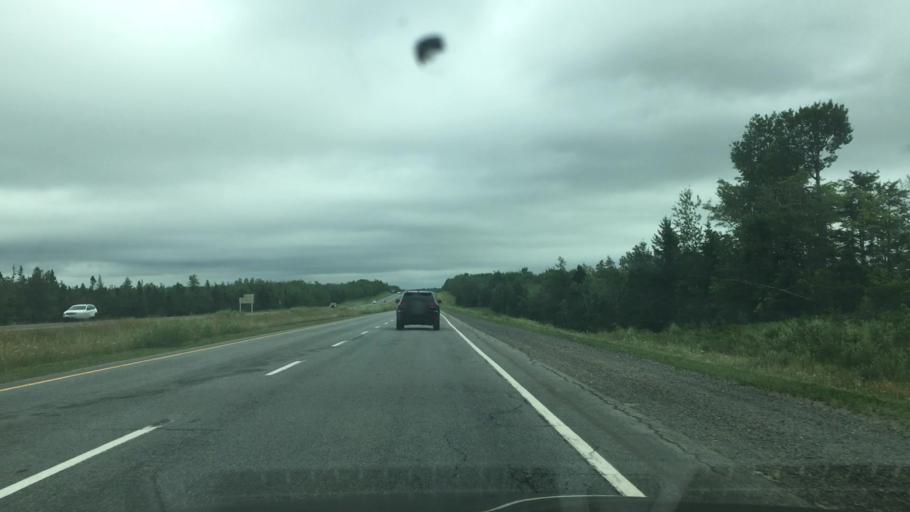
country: CA
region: Nova Scotia
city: Cole Harbour
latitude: 44.9953
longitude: -63.4921
